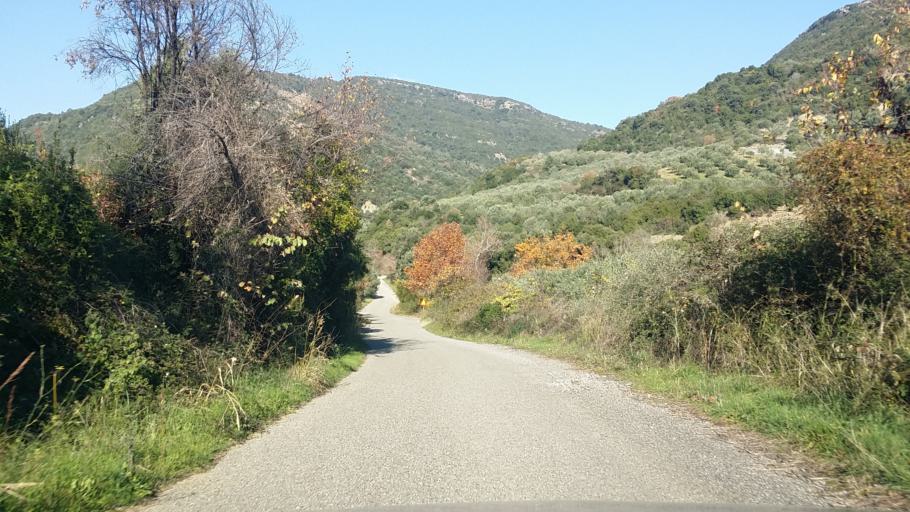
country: GR
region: West Greece
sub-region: Nomos Aitolias kai Akarnanias
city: Krikellos
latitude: 38.9849
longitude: 21.2118
